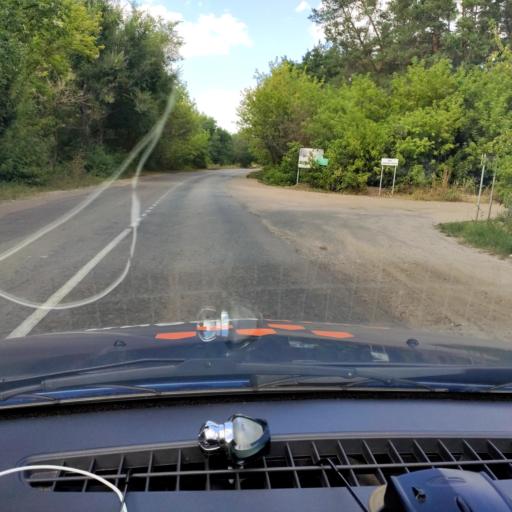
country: RU
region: Voronezj
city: Somovo
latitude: 51.7138
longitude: 39.3669
